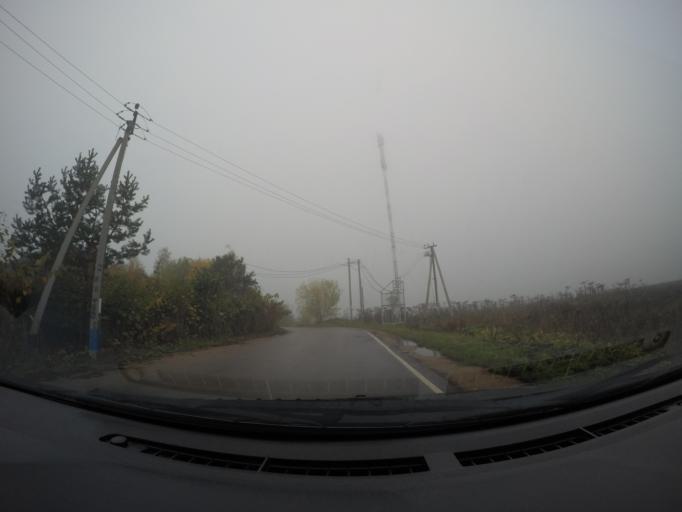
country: RU
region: Moskovskaya
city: Ruza
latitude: 55.7926
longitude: 36.2495
